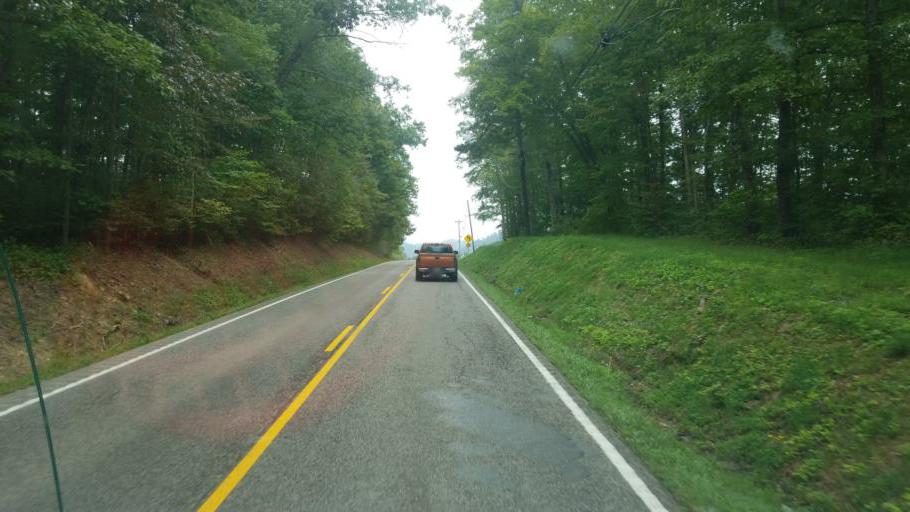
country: US
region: Kentucky
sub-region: Rowan County
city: Morehead
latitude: 38.2307
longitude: -83.4572
